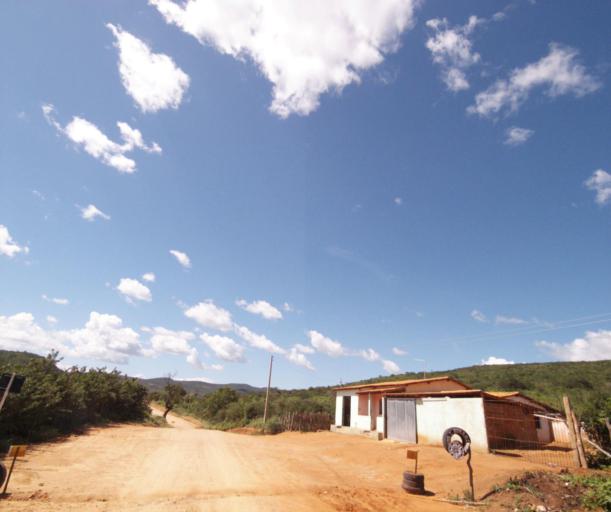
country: BR
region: Bahia
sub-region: Pocoes
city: Pocoes
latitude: -14.2705
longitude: -40.6940
